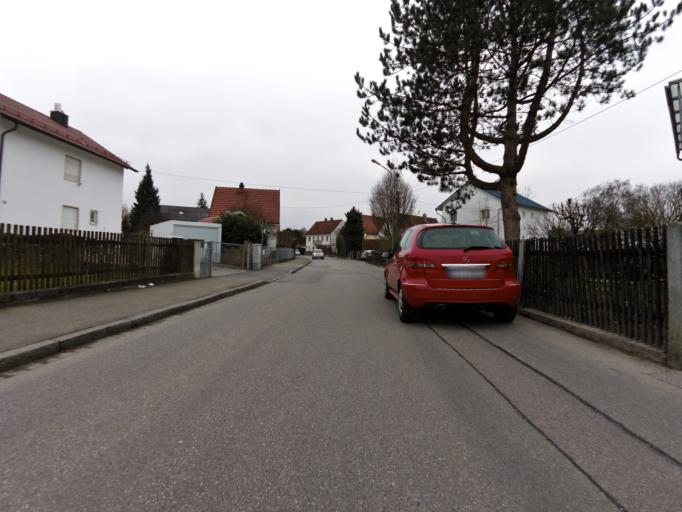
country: DE
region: Bavaria
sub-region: Upper Bavaria
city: Moosburg
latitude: 48.4678
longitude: 11.9427
